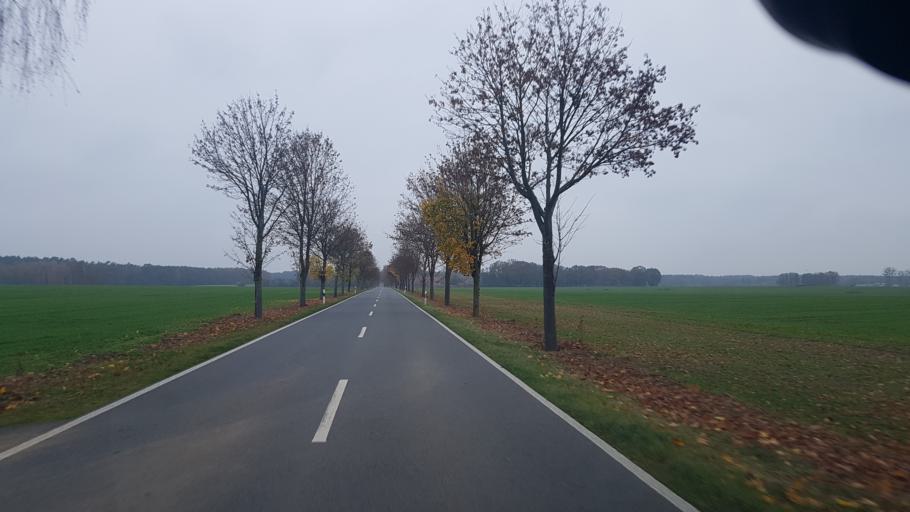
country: DE
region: Brandenburg
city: Lindow
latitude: 52.9453
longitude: 13.0125
